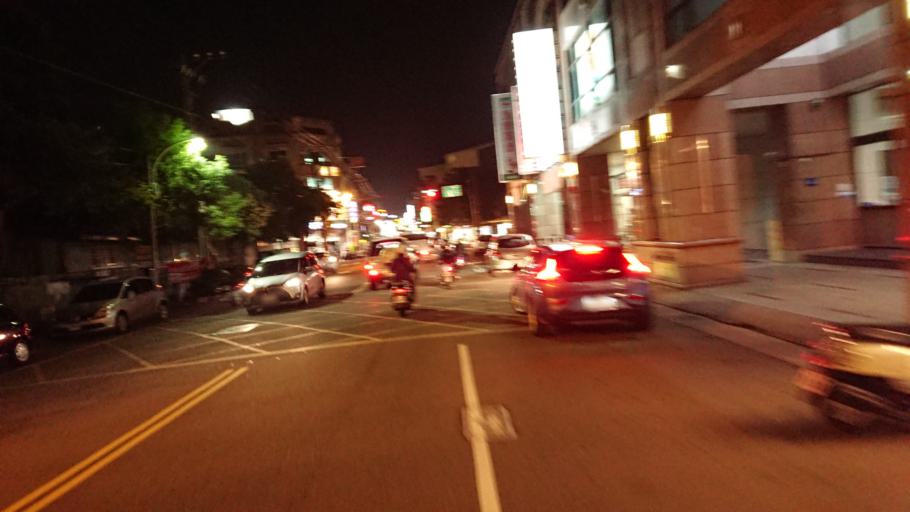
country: TW
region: Taiwan
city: Fengyuan
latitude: 24.2477
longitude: 120.7233
